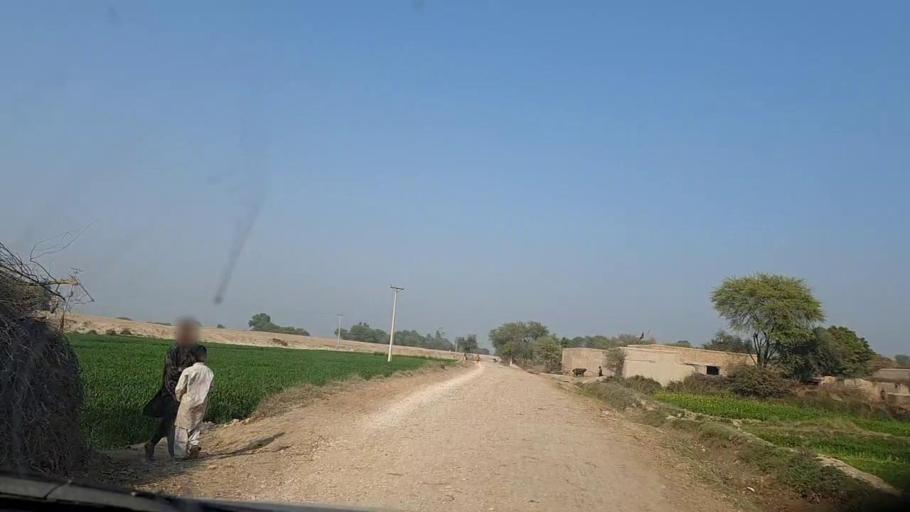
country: PK
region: Sindh
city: Moro
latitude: 26.8017
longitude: 67.9472
